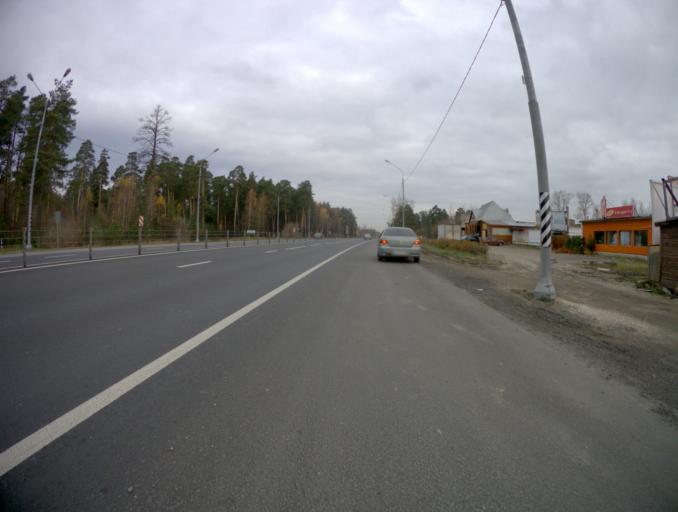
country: RU
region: Moskovskaya
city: Malaya Dubna
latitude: 55.8441
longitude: 38.9655
